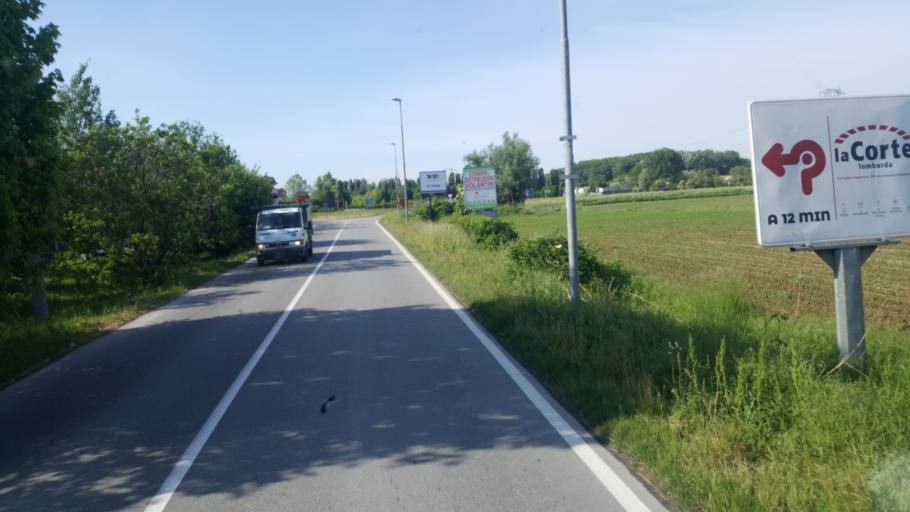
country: IT
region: Lombardy
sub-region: Citta metropolitana di Milano
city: Liscate
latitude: 45.4849
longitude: 9.4044
